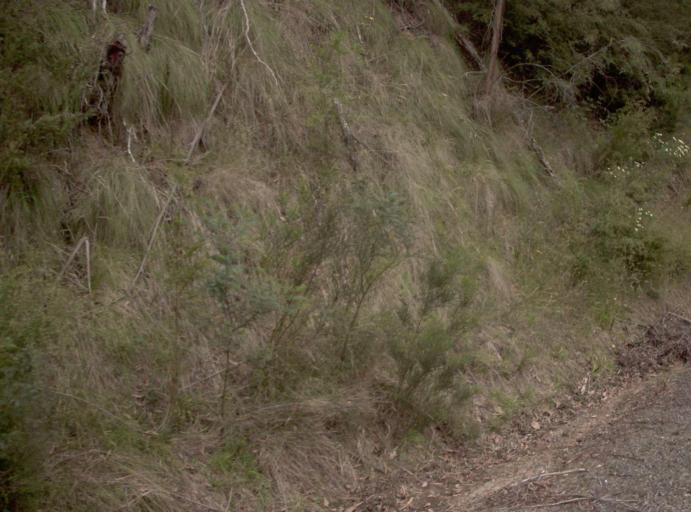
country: AU
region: New South Wales
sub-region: Bombala
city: Bombala
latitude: -37.3761
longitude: 149.2056
